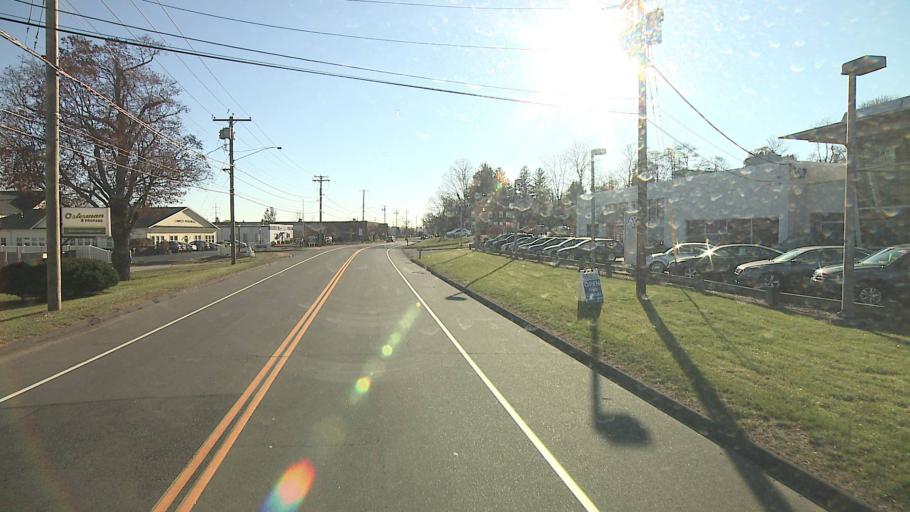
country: US
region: Connecticut
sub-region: New Haven County
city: Hamden
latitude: 41.3631
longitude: -72.8876
